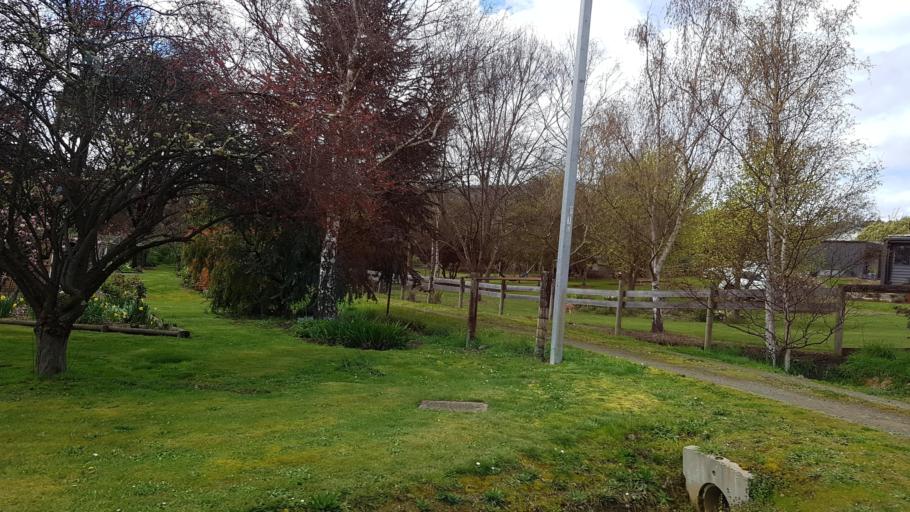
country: AU
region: Tasmania
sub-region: Huon Valley
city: Huonville
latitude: -42.9999
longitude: 147.0656
